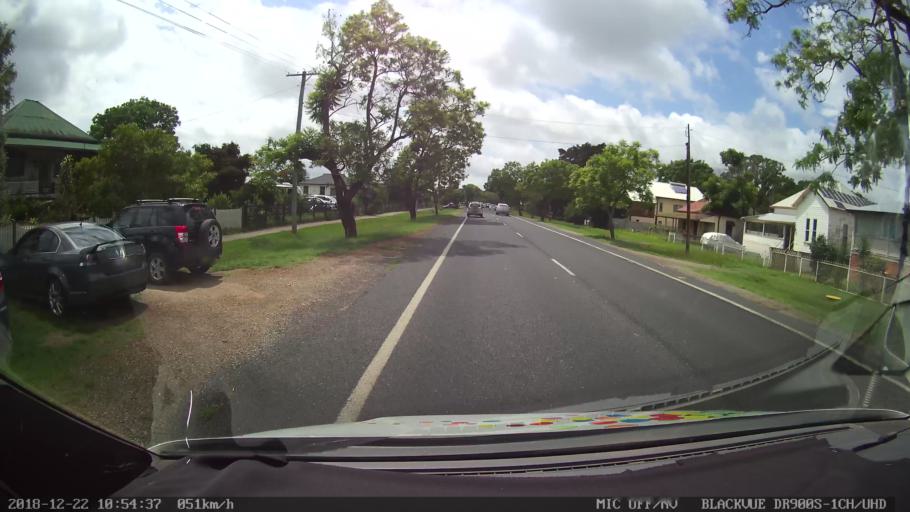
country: AU
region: New South Wales
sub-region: Clarence Valley
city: South Grafton
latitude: -29.7012
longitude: 152.9256
